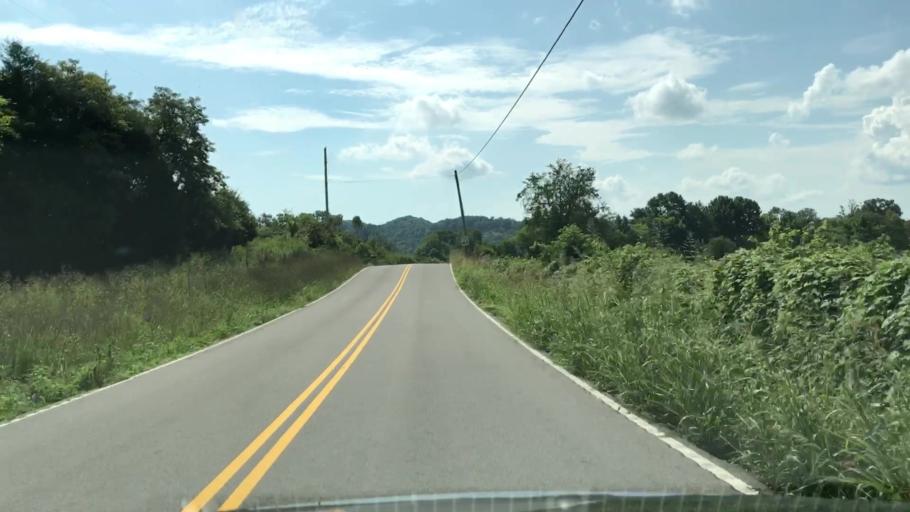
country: US
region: Tennessee
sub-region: Trousdale County
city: Hartsville
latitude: 36.4725
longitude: -86.1796
